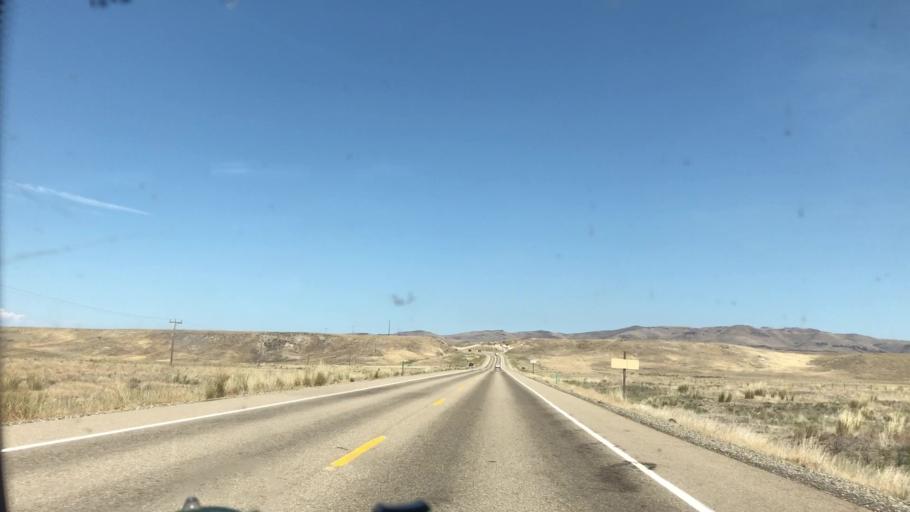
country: US
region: Idaho
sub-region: Owyhee County
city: Marsing
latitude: 43.2574
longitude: -117.0156
